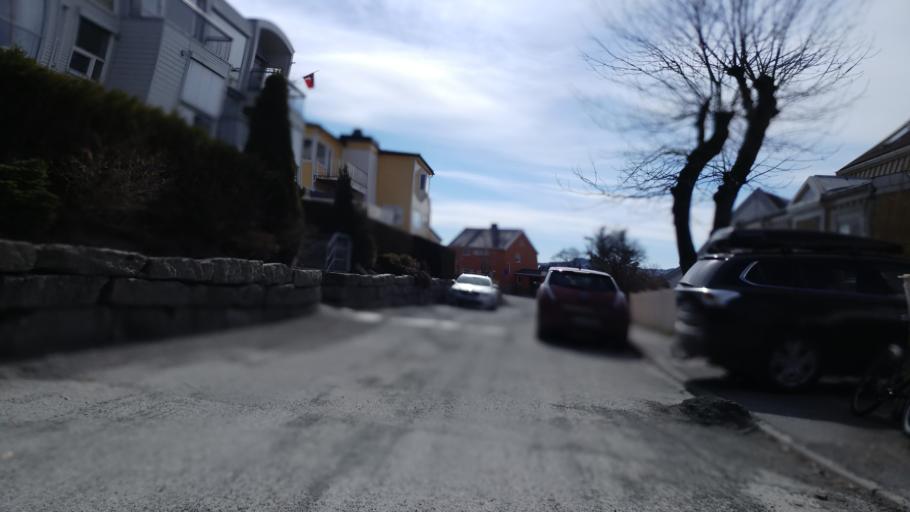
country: NO
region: Sor-Trondelag
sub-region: Trondheim
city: Trondheim
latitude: 63.4303
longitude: 10.4255
